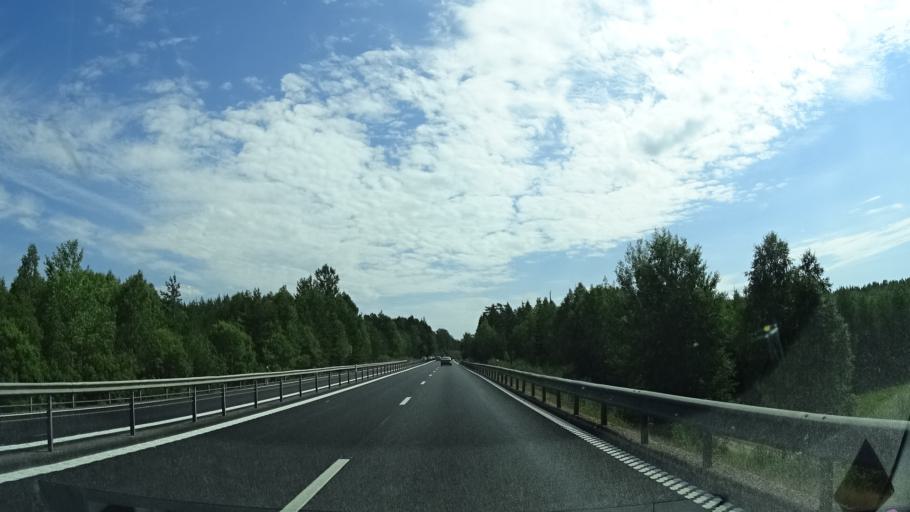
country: SE
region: Vaermland
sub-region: Karlstads Kommun
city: Skattkarr
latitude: 59.4179
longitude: 13.7226
